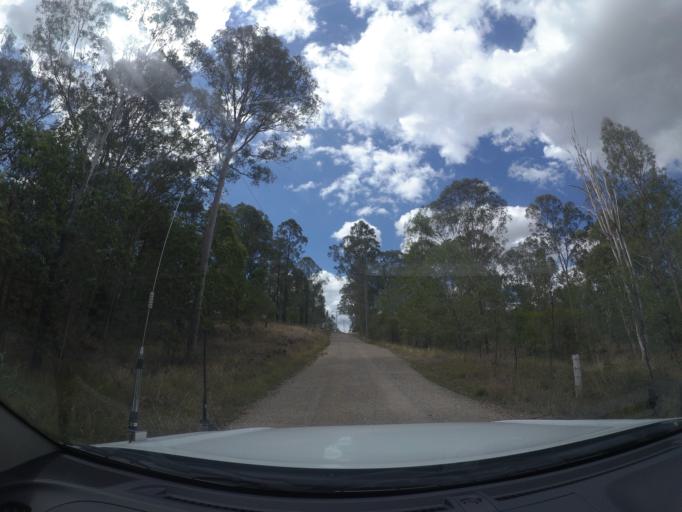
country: AU
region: Queensland
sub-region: Logan
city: Cedar Vale
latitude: -27.8990
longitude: 153.0007
